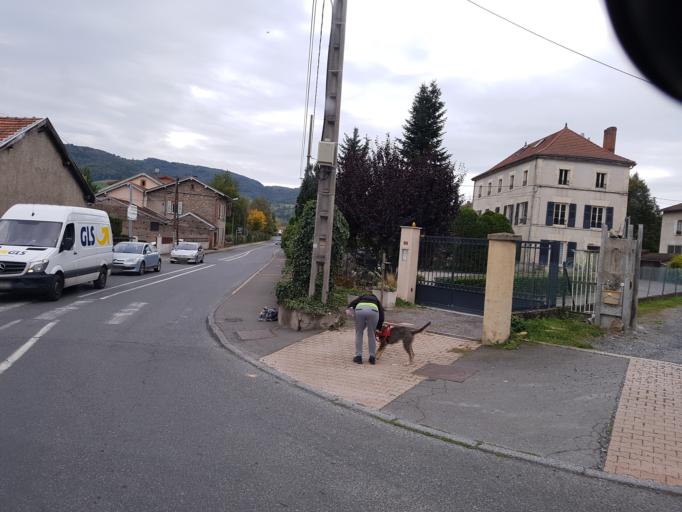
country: FR
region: Rhone-Alpes
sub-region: Departement du Rhone
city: Sainte-Foy-l'Argentiere
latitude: 45.7098
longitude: 4.4666
